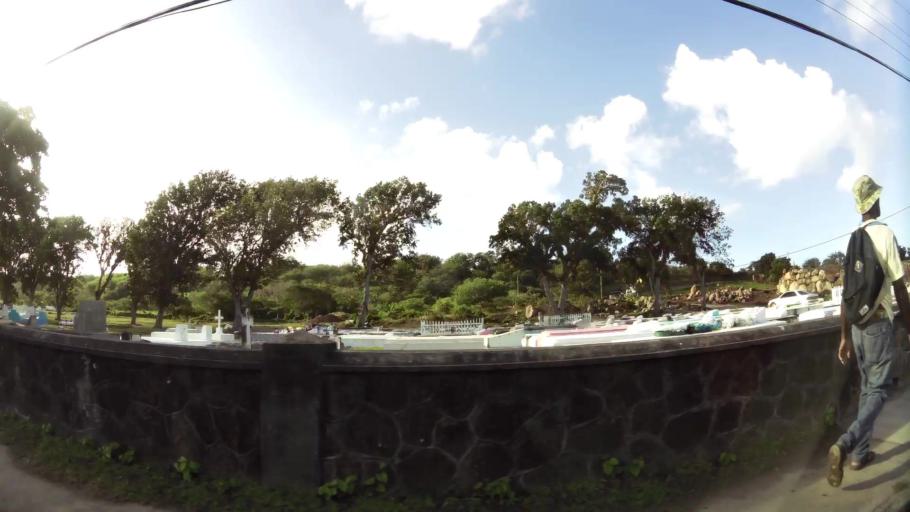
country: KN
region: Saint Paul Charlestown
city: Charlestown
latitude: 17.1314
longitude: -62.6213
